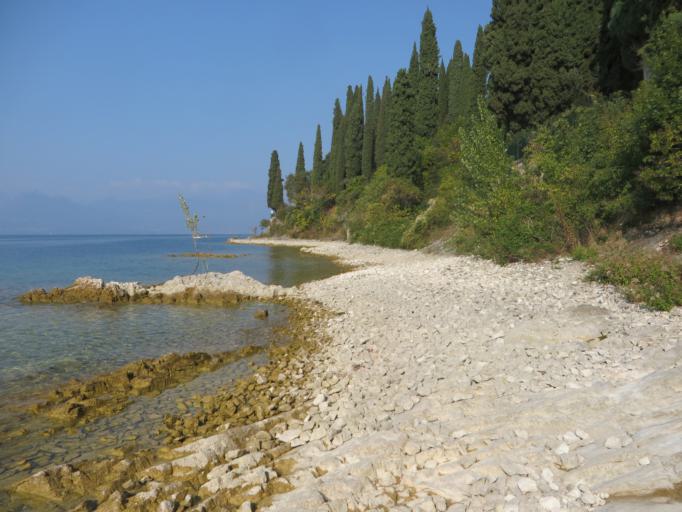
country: IT
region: Veneto
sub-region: Provincia di Verona
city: Torri del Benaco
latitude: 45.5787
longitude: 10.6730
